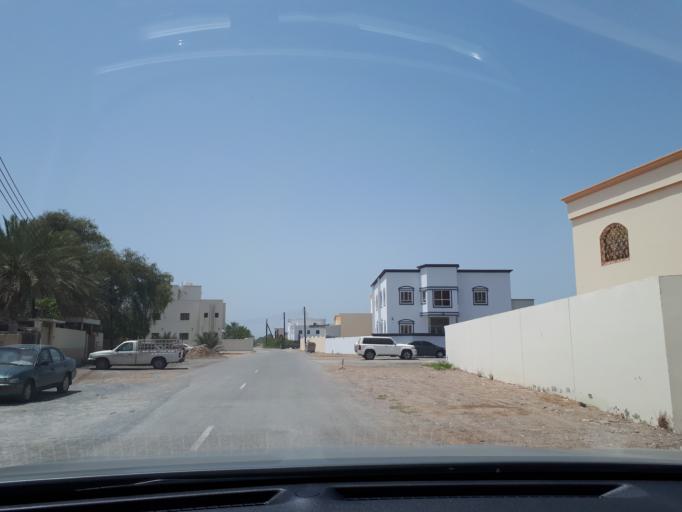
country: OM
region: Muhafazat Masqat
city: As Sib al Jadidah
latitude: 23.6884
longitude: 58.1119
